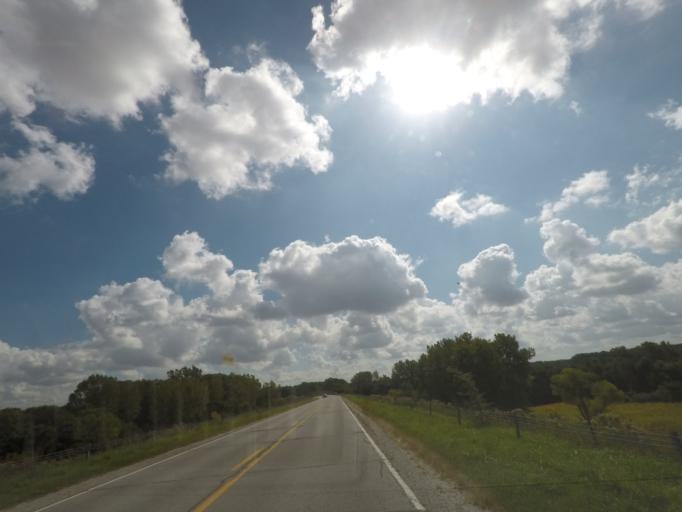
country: US
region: Iowa
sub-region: Story County
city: Nevada
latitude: 42.0217
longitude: -93.3961
